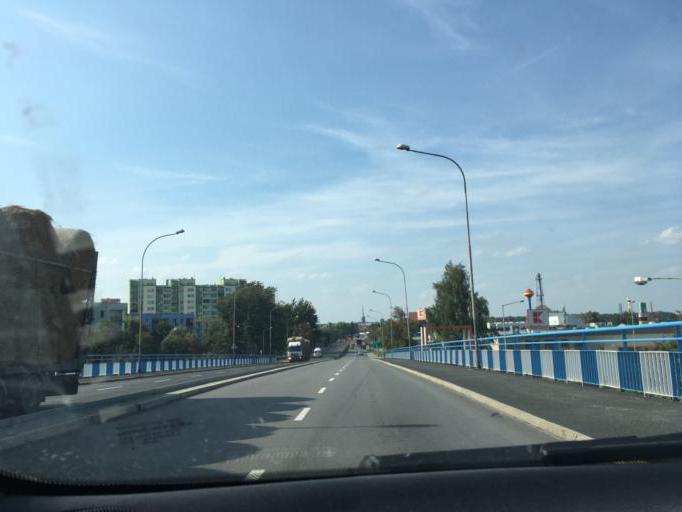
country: PL
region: Opole Voivodeship
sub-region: Powiat nyski
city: Nysa
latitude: 50.4632
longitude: 17.3457
